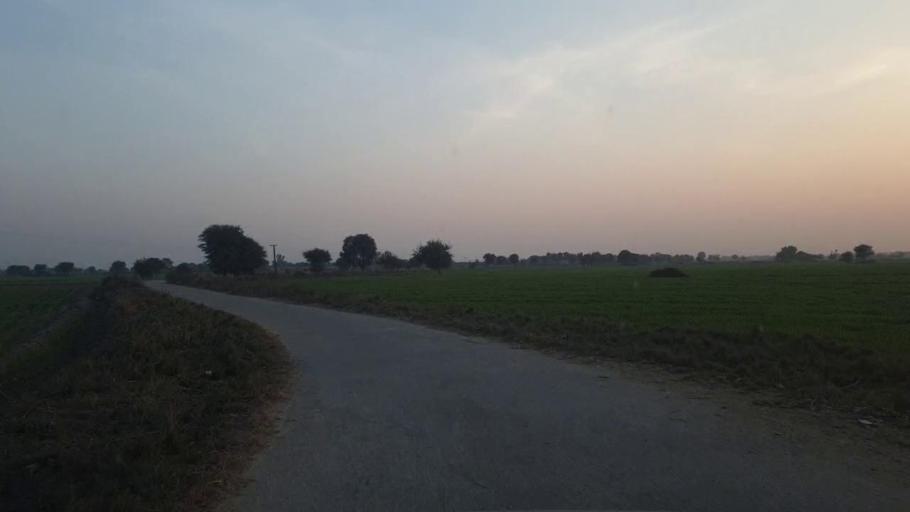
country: PK
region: Sindh
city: Bhit Shah
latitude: 25.8574
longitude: 68.5141
